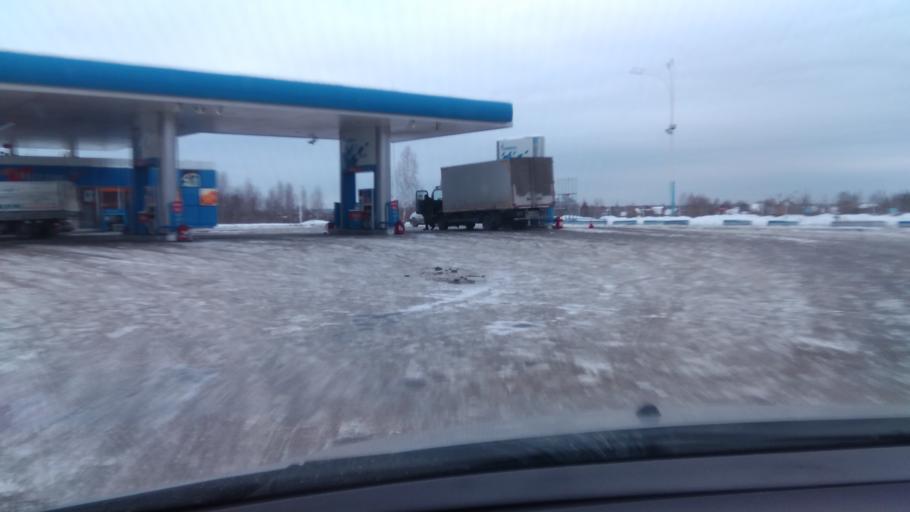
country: RU
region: Sverdlovsk
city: Istok
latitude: 56.7060
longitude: 60.7456
